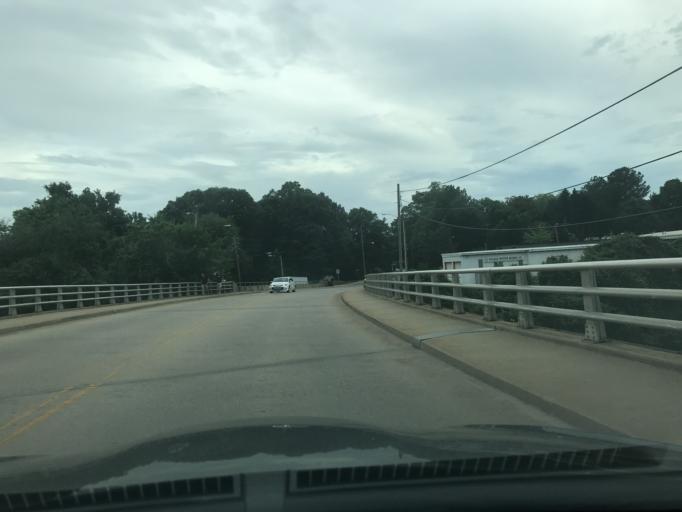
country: US
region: North Carolina
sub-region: Wake County
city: Raleigh
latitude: 35.7778
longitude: -78.6494
